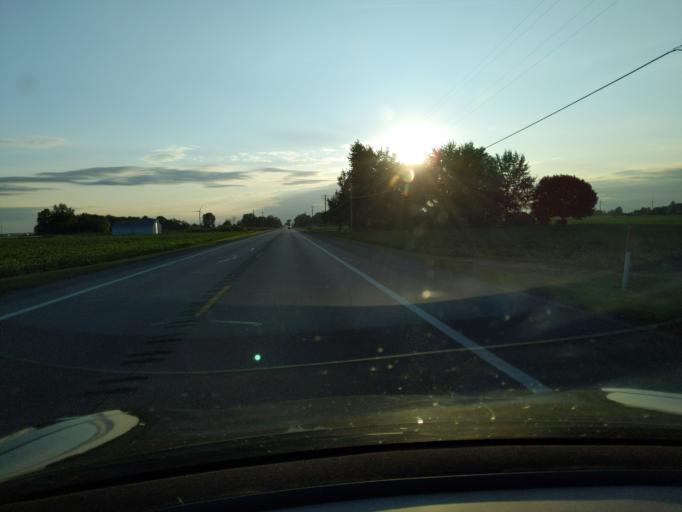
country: US
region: Michigan
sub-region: Gratiot County
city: Breckenridge
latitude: 43.4080
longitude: -84.4932
